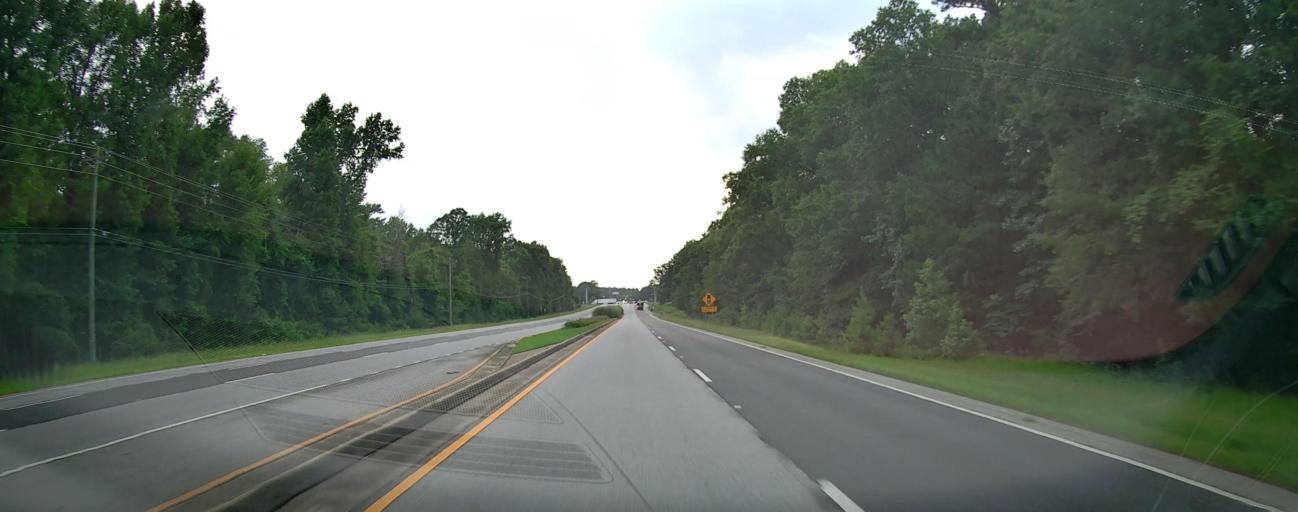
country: US
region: Georgia
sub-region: Muscogee County
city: Columbus
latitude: 32.5395
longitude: -84.8348
